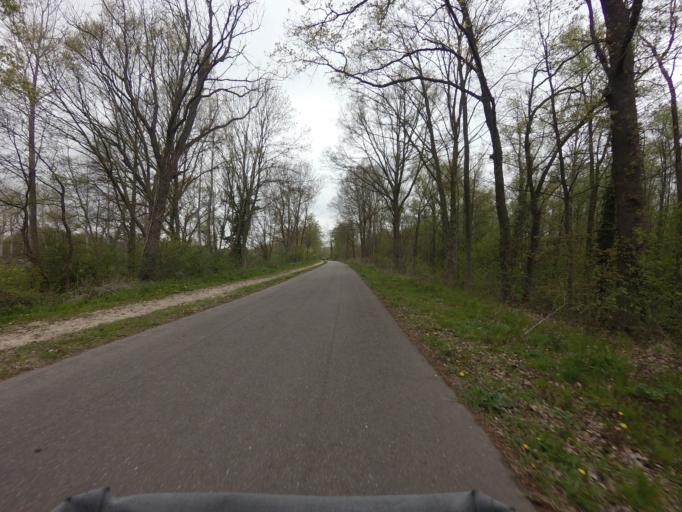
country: NL
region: Limburg
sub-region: Gemeente Schinnen
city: Schinnen
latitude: 50.9381
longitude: 5.8864
